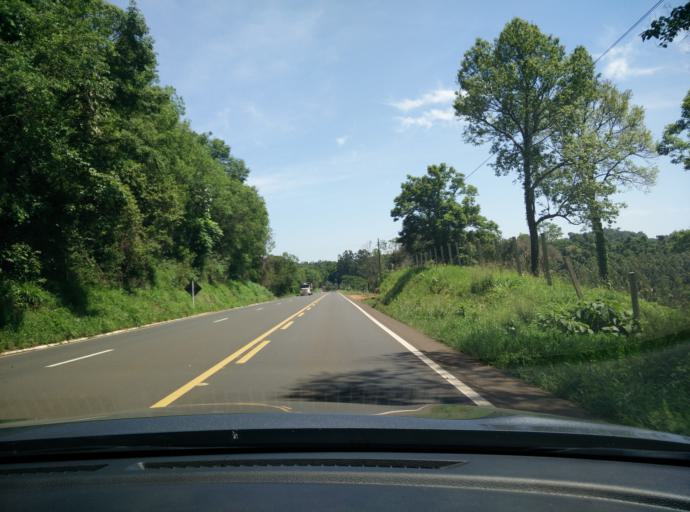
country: BR
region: Parana
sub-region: Santo Antonio Do Sudoeste
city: Santo Antonio do Sudoeste
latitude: -25.8539
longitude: -53.7452
